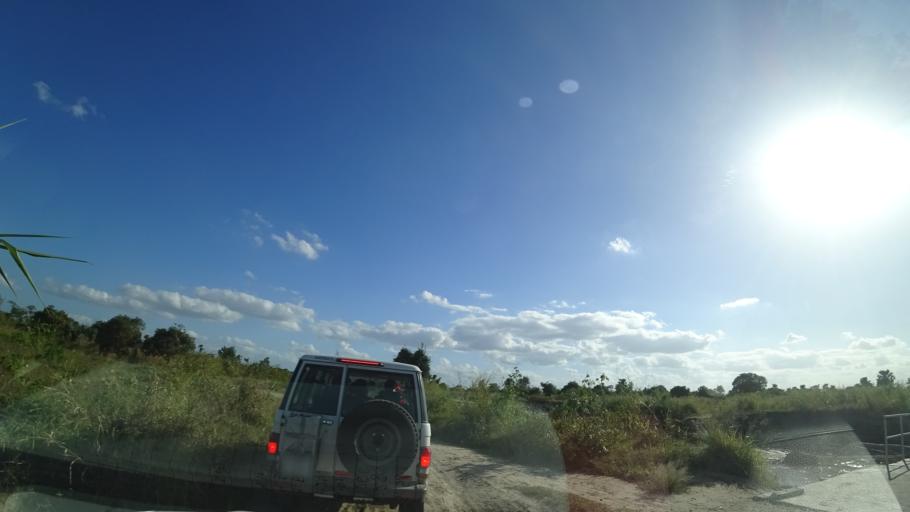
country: MZ
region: Sofala
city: Dondo
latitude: -19.3601
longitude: 34.5882
